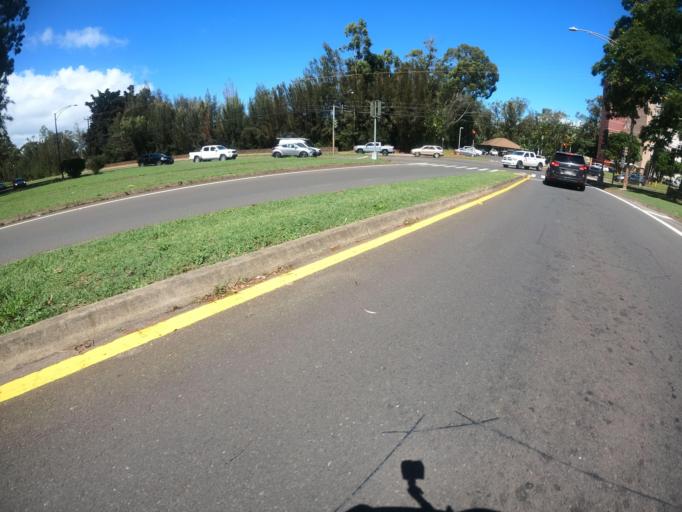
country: US
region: Hawaii
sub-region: Honolulu County
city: Wahiawa
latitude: 21.4884
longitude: -158.0397
